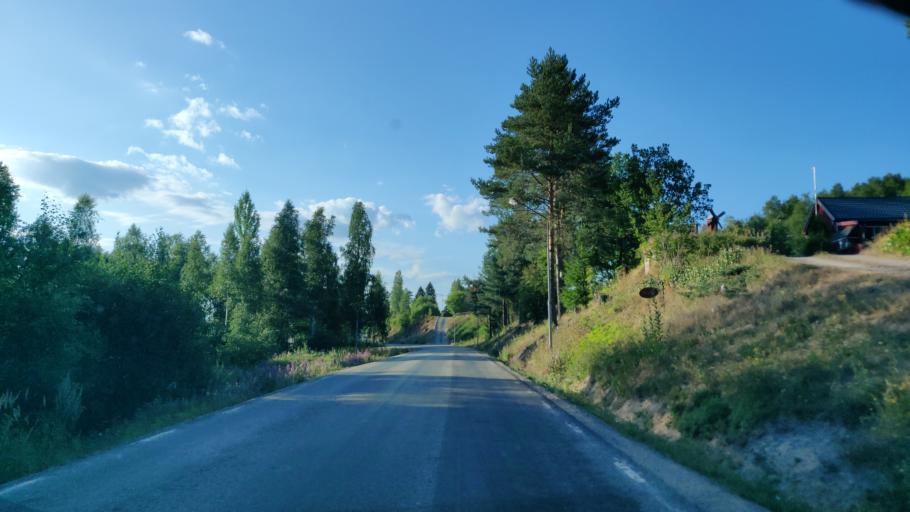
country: SE
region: Vaermland
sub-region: Hagfors Kommun
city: Ekshaerad
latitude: 60.1800
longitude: 13.5263
